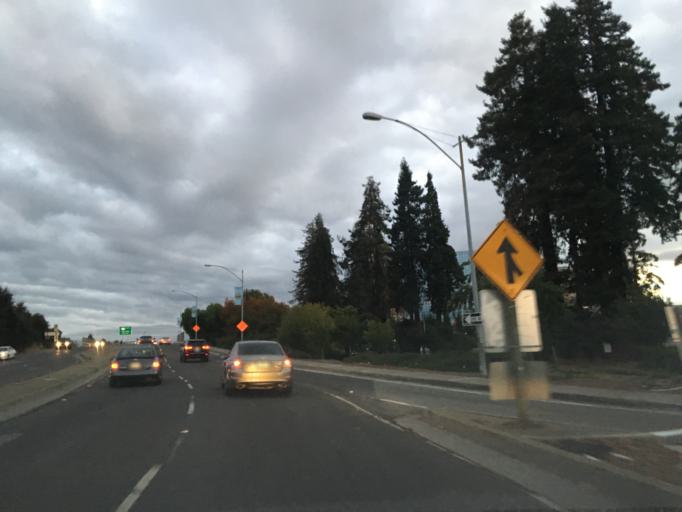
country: US
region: California
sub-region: San Mateo County
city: East Palo Alto
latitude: 37.4626
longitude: -122.1419
